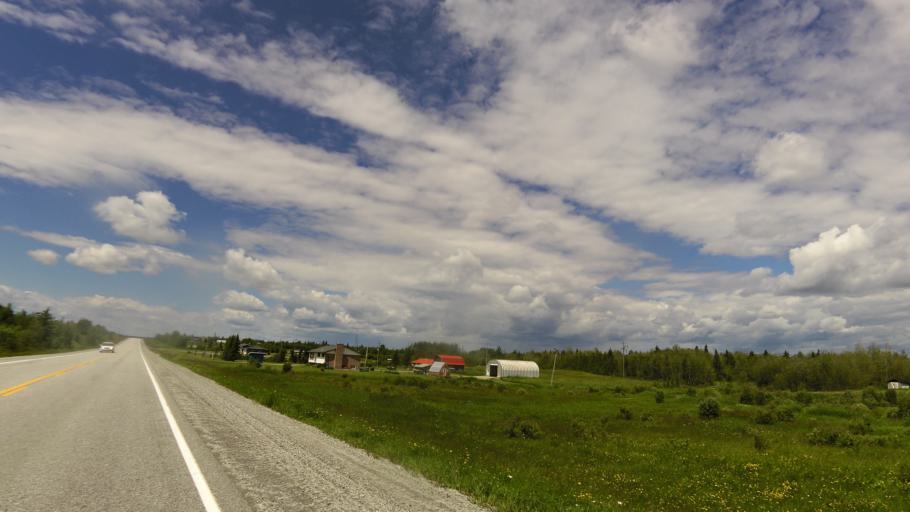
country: CA
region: Ontario
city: Kapuskasing
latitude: 49.3037
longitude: -81.9971
